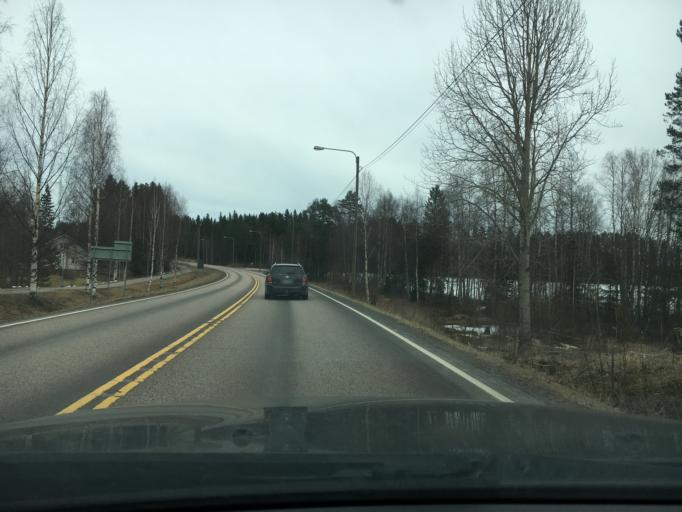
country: FI
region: Central Finland
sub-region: AEaenekoski
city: Konnevesi
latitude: 62.6304
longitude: 26.3224
